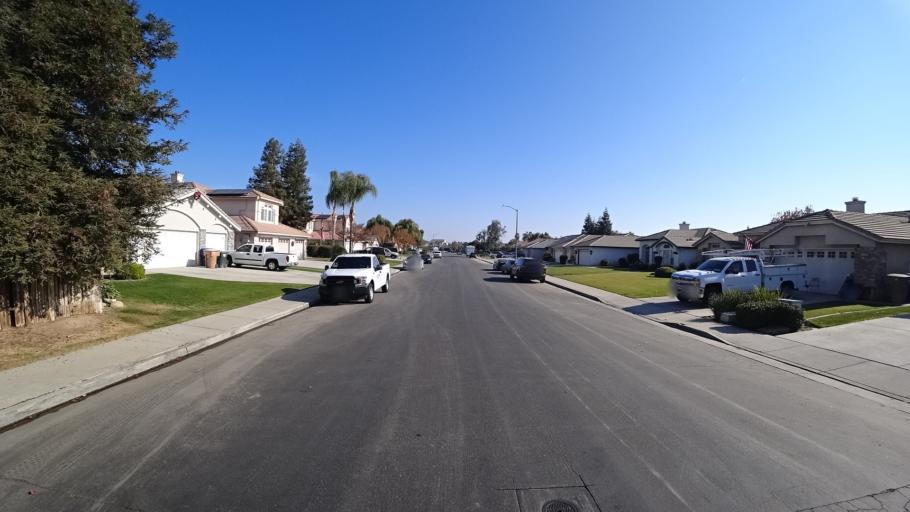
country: US
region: California
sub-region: Kern County
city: Greenacres
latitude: 35.3155
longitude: -119.1259
